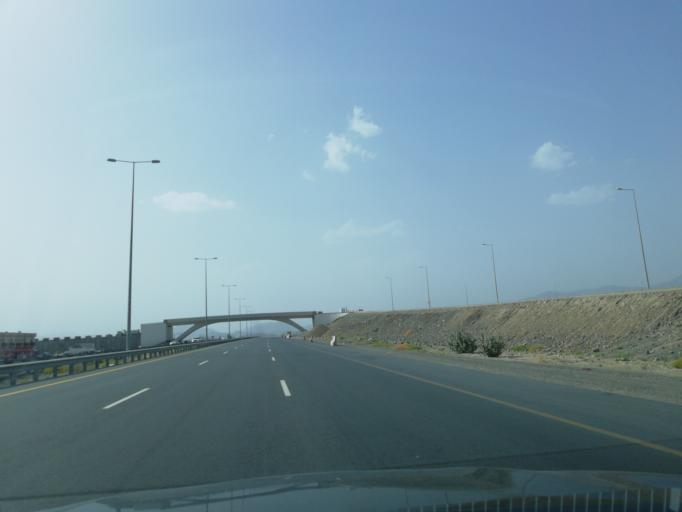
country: OM
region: Muhafazat ad Dakhiliyah
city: Sufalat Sama'il
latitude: 23.0392
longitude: 58.2008
